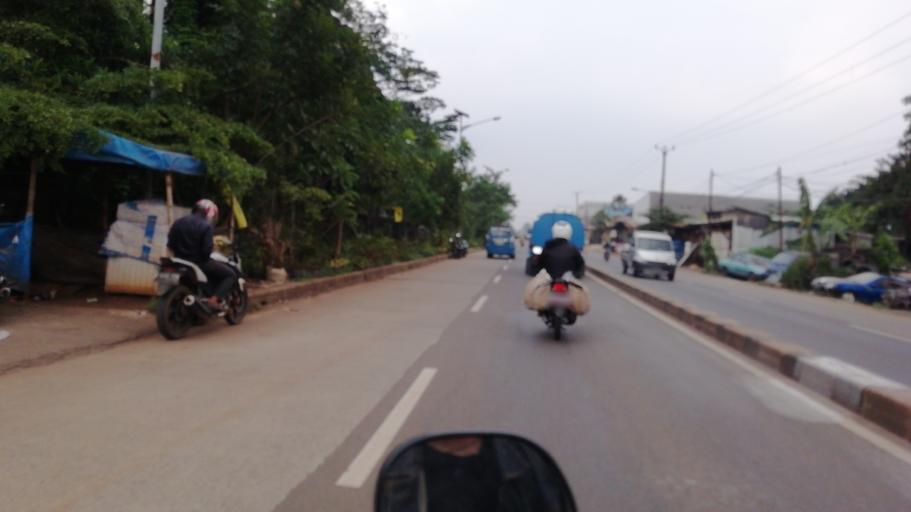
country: ID
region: West Java
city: Parung
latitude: -6.4571
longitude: 106.7307
